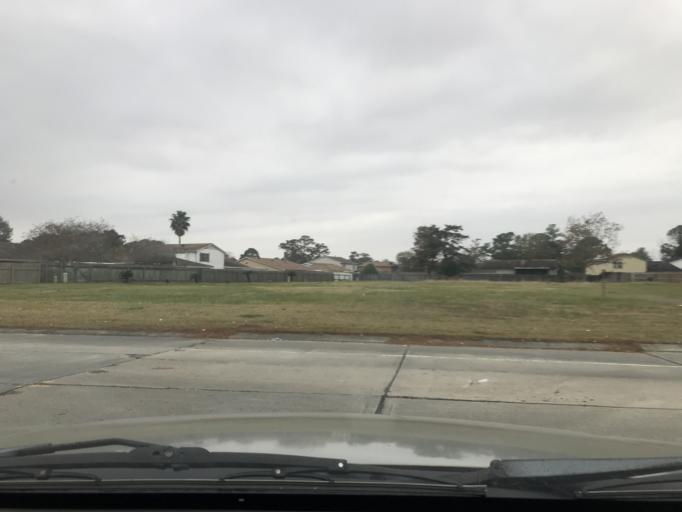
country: US
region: Louisiana
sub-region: Jefferson Parish
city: Woodmere
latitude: 29.8639
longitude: -90.0757
